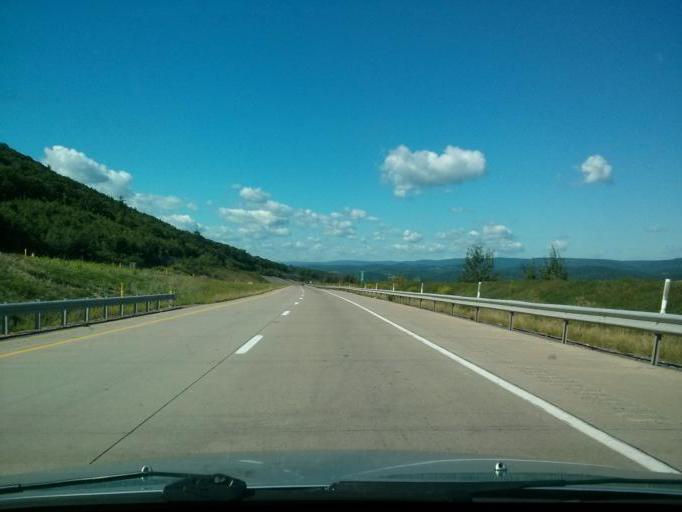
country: US
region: Pennsylvania
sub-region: Centre County
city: Stormstown
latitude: 40.8289
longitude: -77.9912
